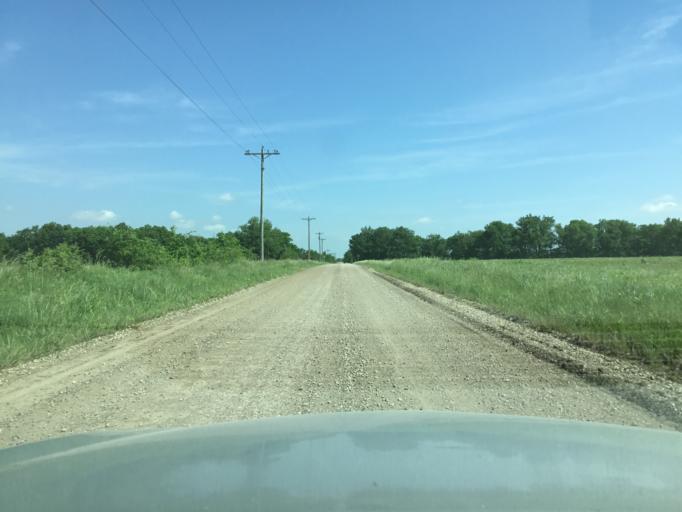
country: US
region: Kansas
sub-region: Labette County
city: Oswego
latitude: 37.1689
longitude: -95.1399
